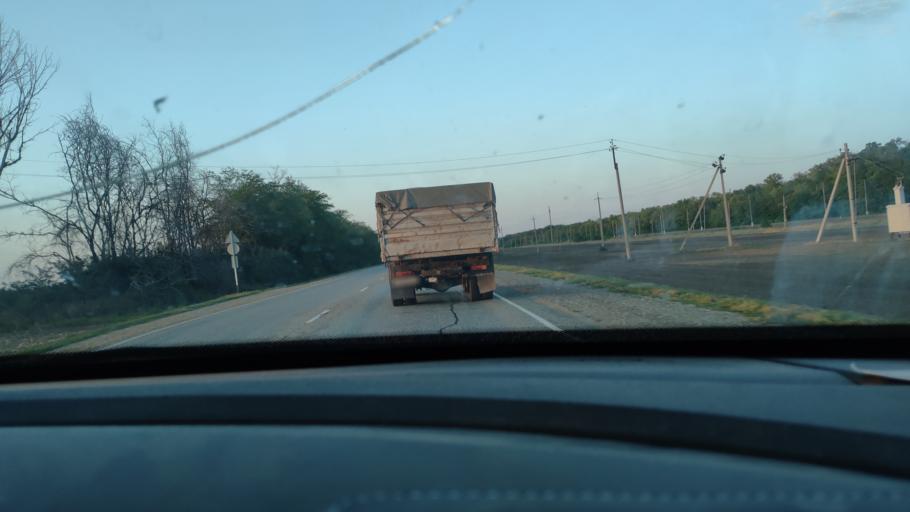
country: RU
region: Krasnodarskiy
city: Starominskaya
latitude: 46.4775
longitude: 39.0492
